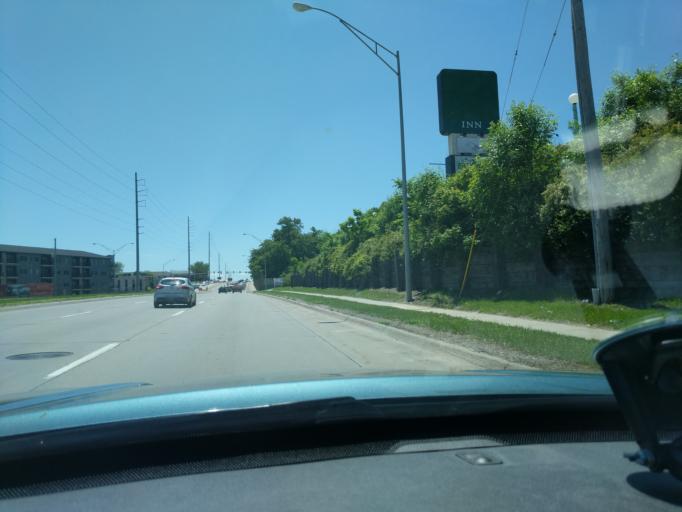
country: US
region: Nebraska
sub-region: Douglas County
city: Ralston
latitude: 41.2333
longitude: -96.0241
